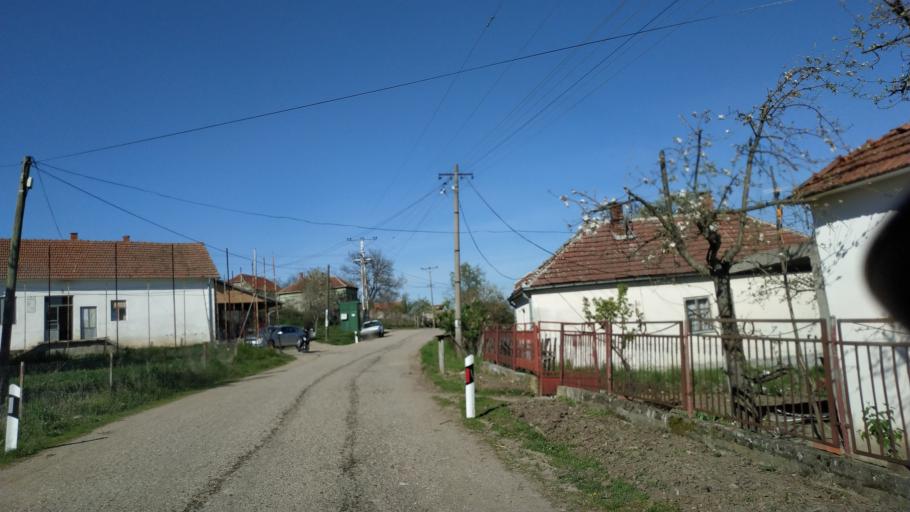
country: RS
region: Central Serbia
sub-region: Nisavski Okrug
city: Aleksinac
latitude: 43.4838
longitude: 21.6560
